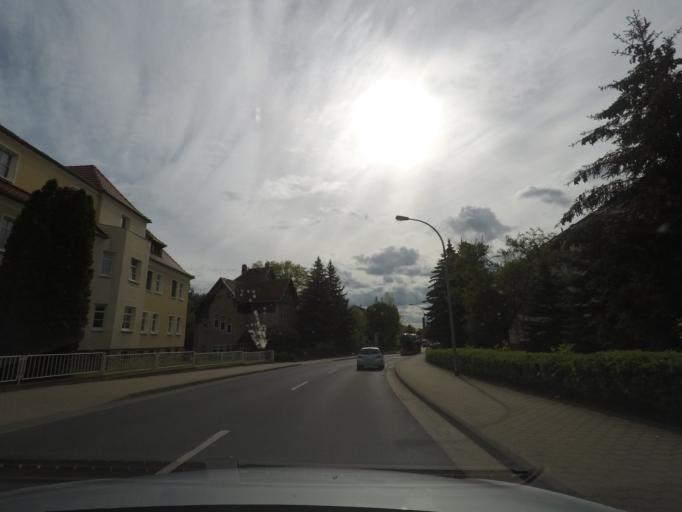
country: DE
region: Saxony
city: Dobeln
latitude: 51.1250
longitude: 13.0946
